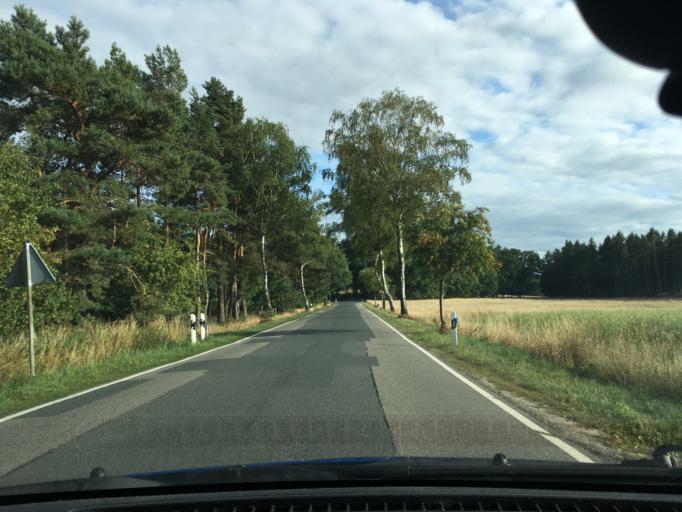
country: DE
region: Lower Saxony
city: Stelle
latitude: 53.3380
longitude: 10.0816
